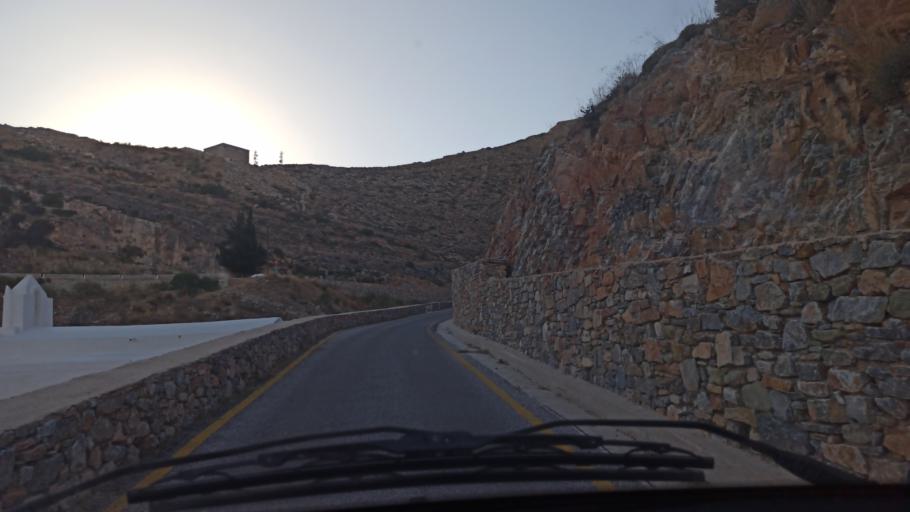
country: GR
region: South Aegean
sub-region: Nomos Kykladon
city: Ano Syros
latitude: 37.4539
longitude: 24.9360
